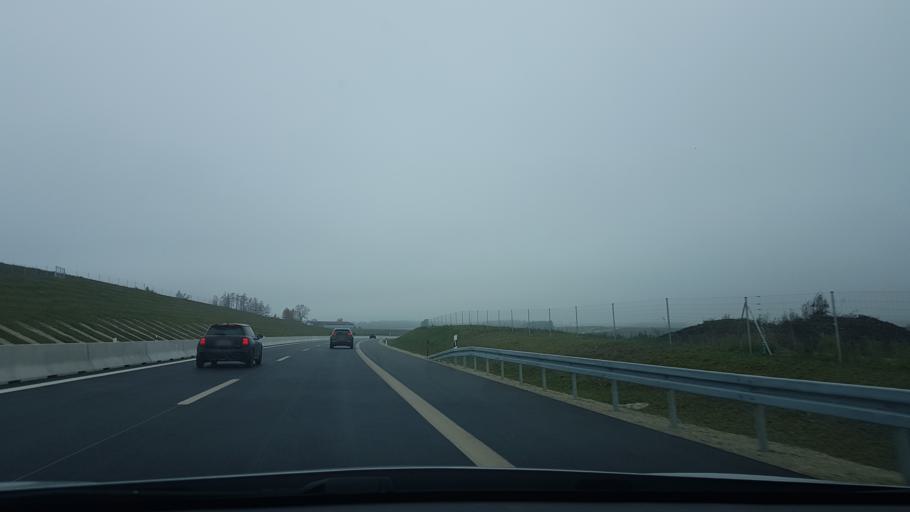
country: DE
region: Bavaria
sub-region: Lower Bavaria
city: Essenbach
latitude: 48.6271
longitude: 12.2127
